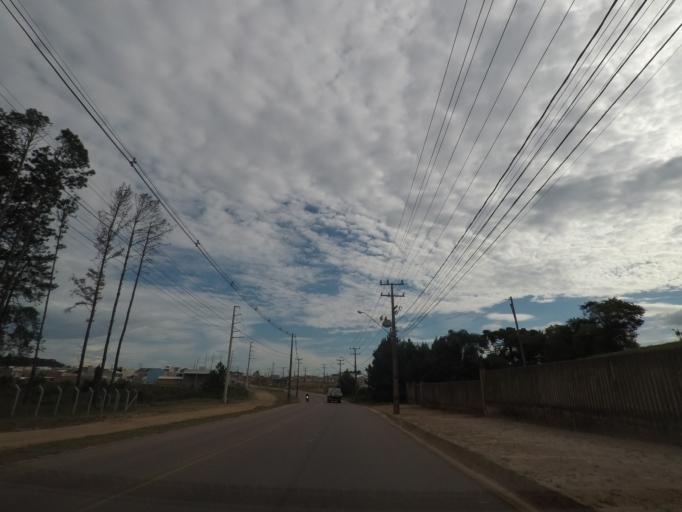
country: BR
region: Parana
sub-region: Araucaria
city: Araucaria
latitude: -25.6306
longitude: -49.2892
